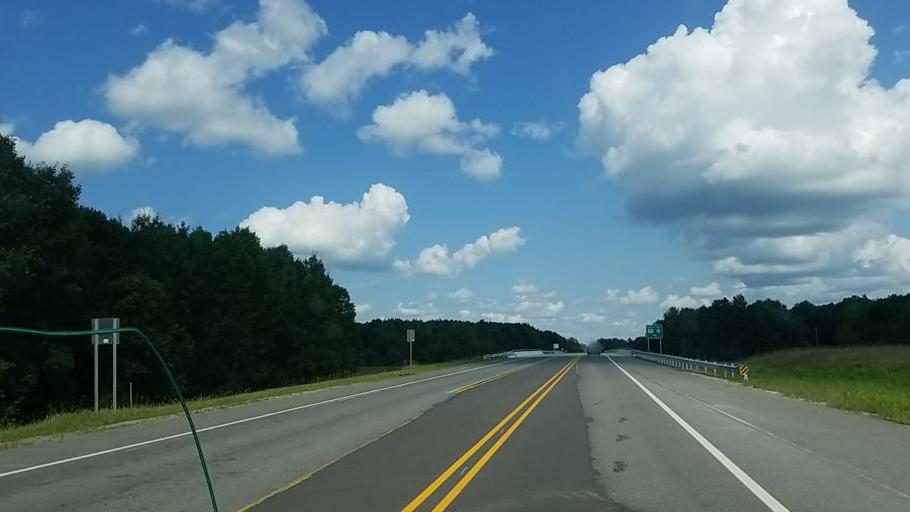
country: US
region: Michigan
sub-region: Montcalm County
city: Howard City
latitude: 43.3957
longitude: -85.5166
